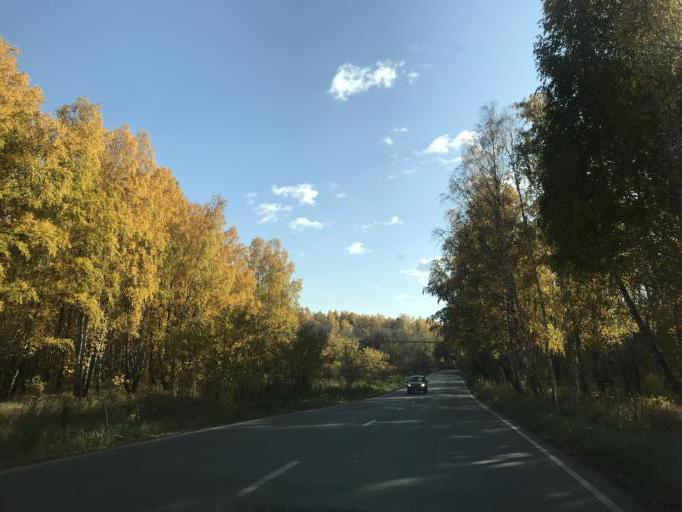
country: RU
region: Chelyabinsk
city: Dolgoderevenskoye
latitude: 55.2649
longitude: 61.3646
